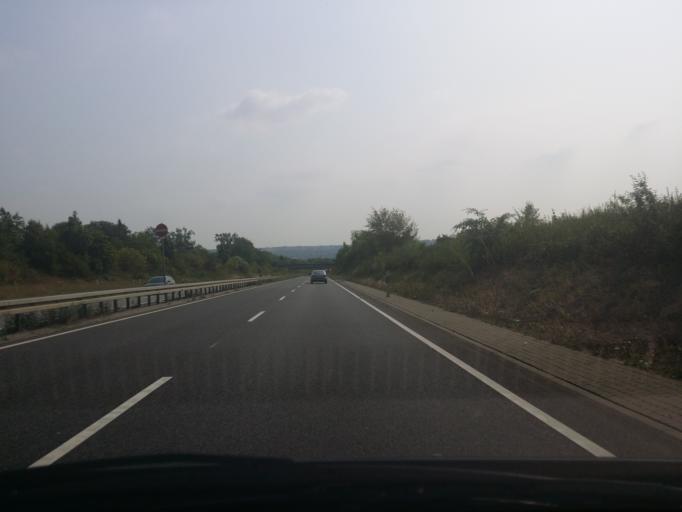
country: DE
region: Hesse
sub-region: Regierungsbezirk Darmstadt
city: Eltville
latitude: 50.0289
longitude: 8.1066
